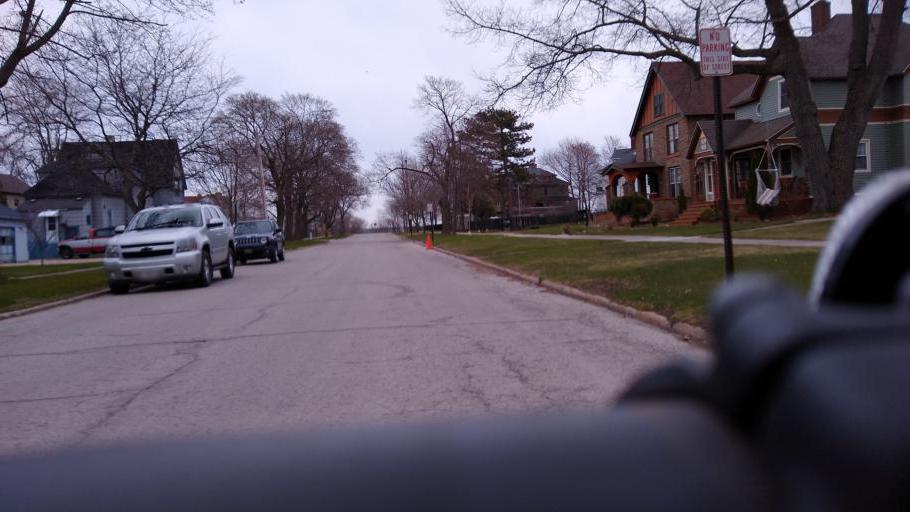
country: US
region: Michigan
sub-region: Delta County
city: Escanaba
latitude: 45.7395
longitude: -87.0581
